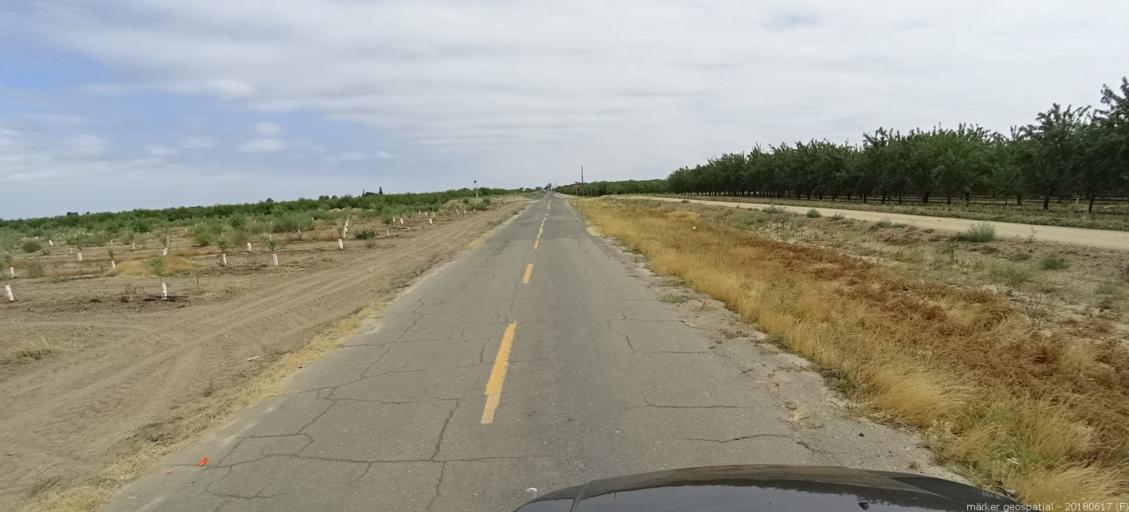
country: US
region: California
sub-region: Madera County
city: Fairmead
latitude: 36.9954
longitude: -120.2205
